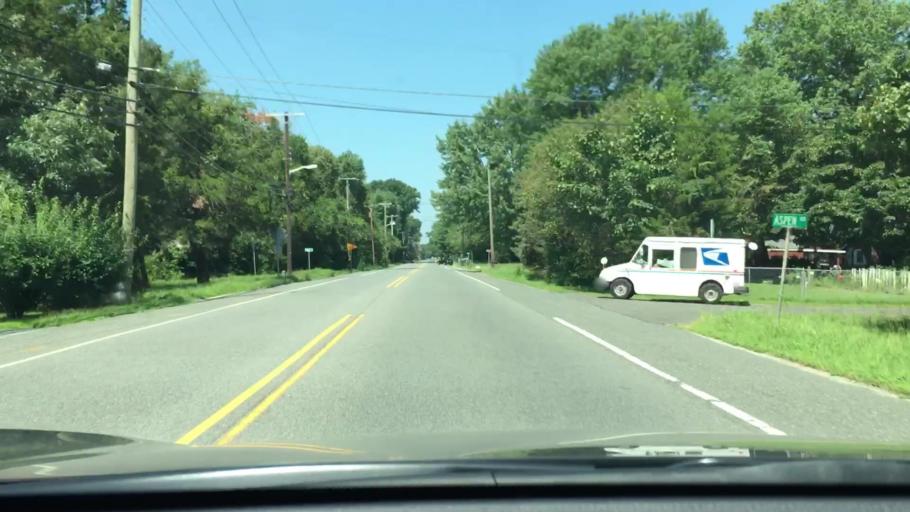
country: US
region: New Jersey
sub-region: Cumberland County
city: Laurel Lake
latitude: 39.3349
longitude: -75.0218
